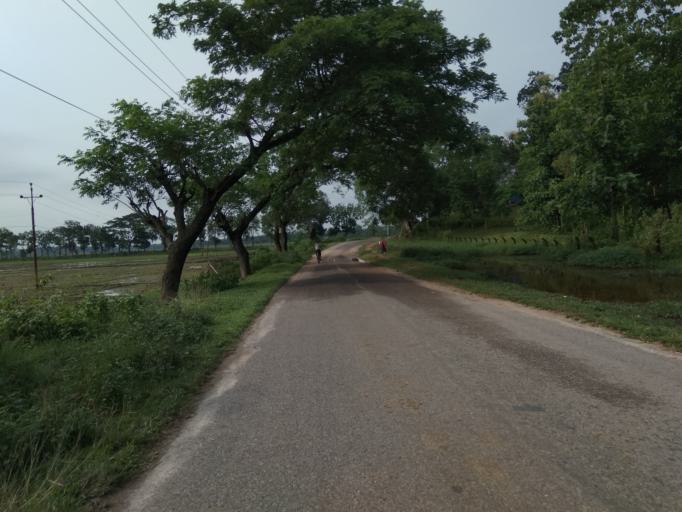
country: BD
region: Chittagong
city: Khagrachhari
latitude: 23.0226
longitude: 92.0152
